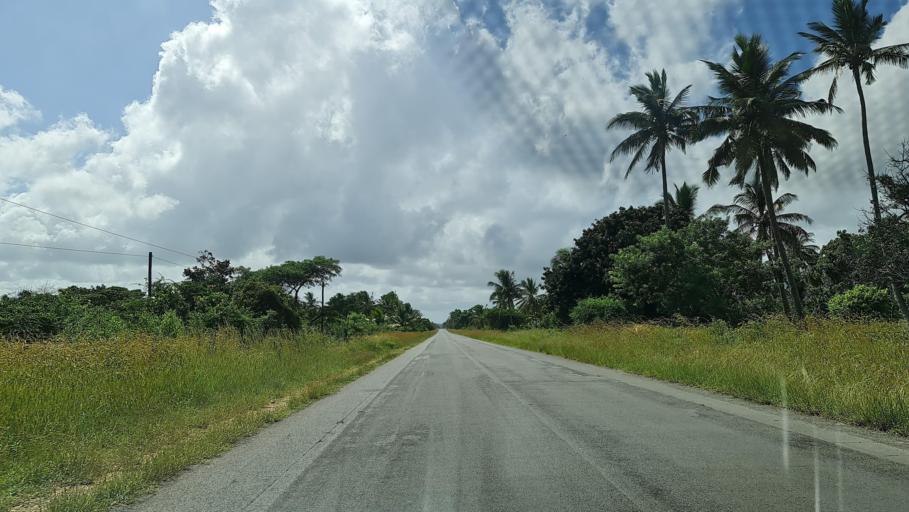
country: MZ
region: Gaza
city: Manjacaze
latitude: -24.6799
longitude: 34.6022
